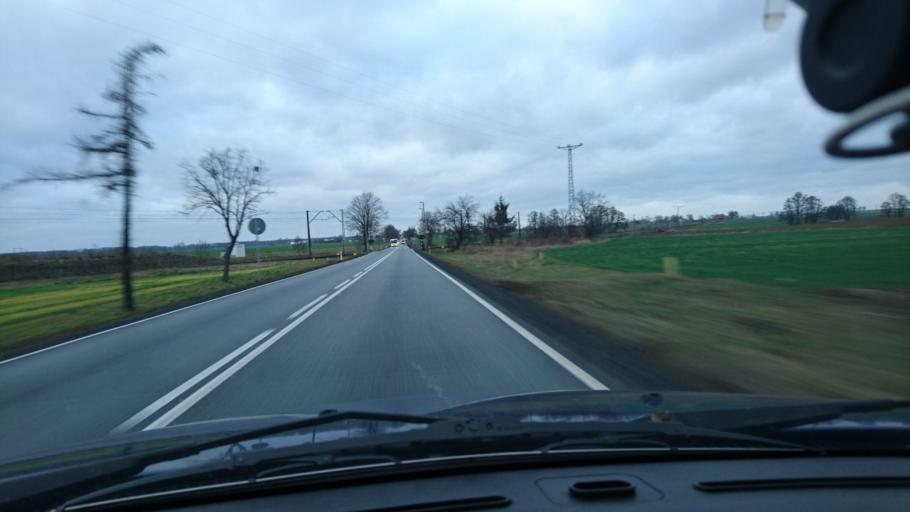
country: PL
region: Opole Voivodeship
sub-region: Powiat kluczborski
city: Kluczbork
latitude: 51.0151
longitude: 18.2006
